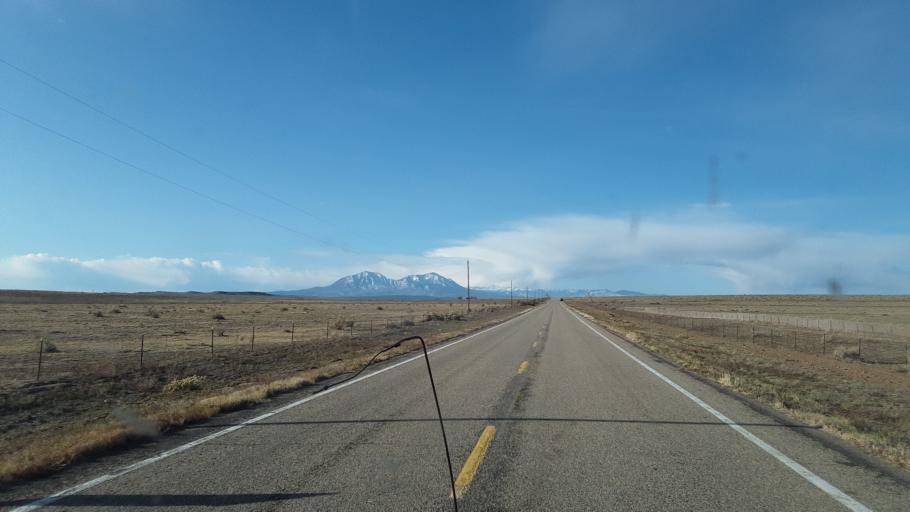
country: US
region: Colorado
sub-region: Huerfano County
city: Walsenburg
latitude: 37.6766
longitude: -104.6593
